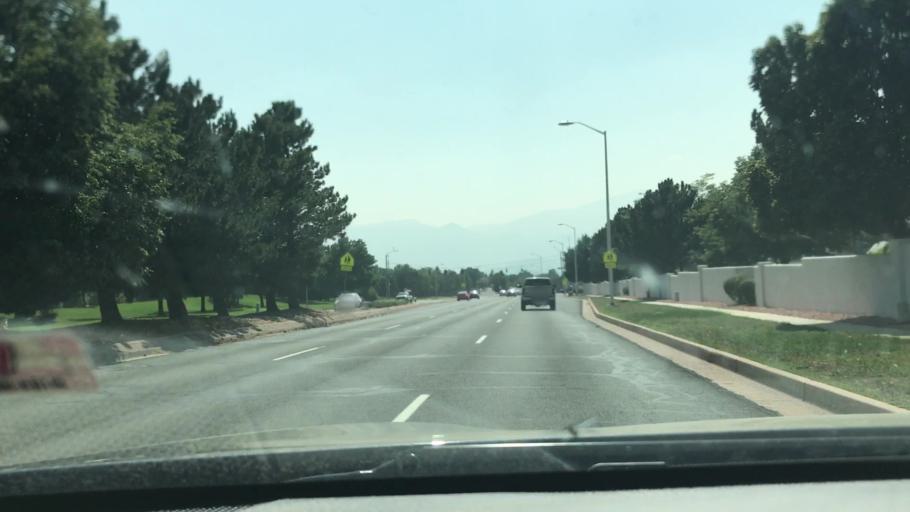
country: US
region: Colorado
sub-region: El Paso County
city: Black Forest
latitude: 38.9496
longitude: -104.7680
